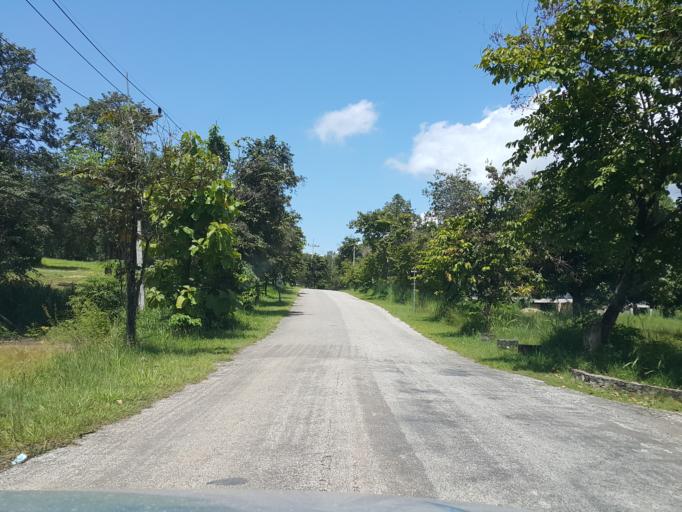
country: TH
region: Chiang Mai
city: San Kamphaeng
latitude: 18.7001
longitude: 99.1763
